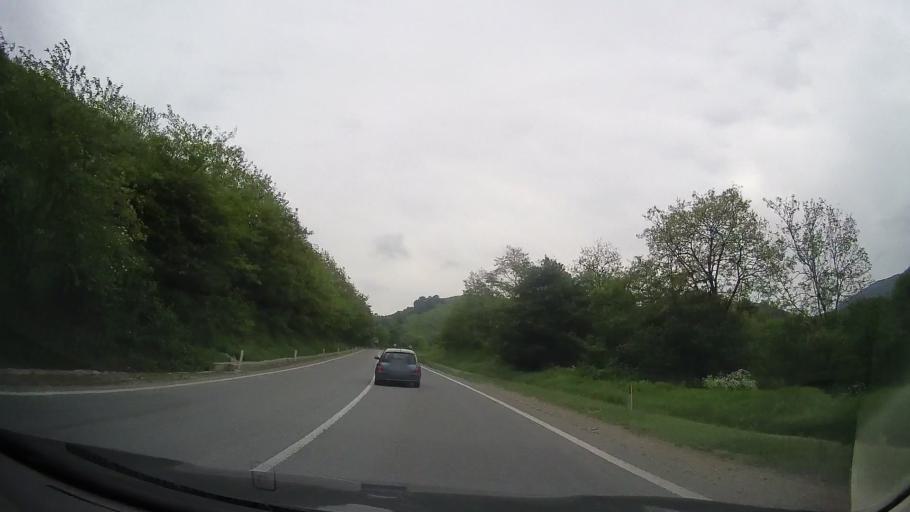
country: RO
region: Caras-Severin
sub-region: Comuna Slatina-Timis
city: Slatina-Timis
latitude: 45.2277
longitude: 22.3035
